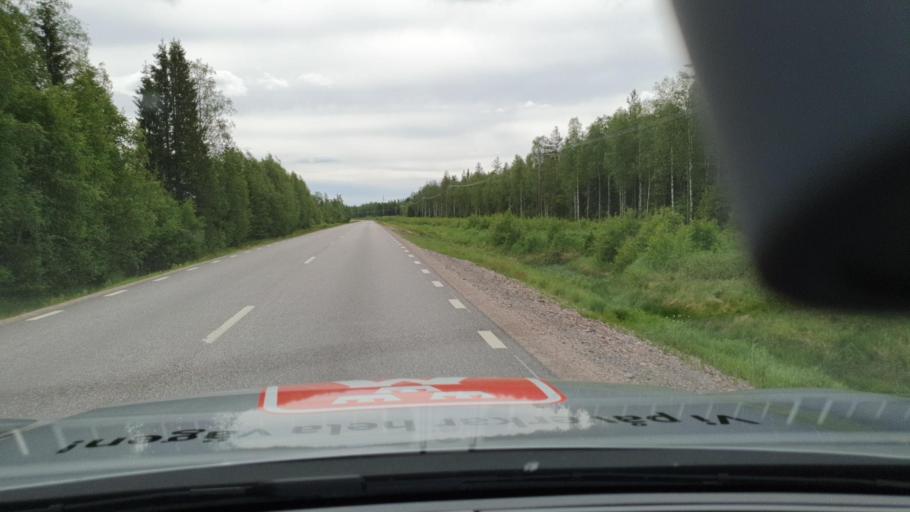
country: SE
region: Norrbotten
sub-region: Kalix Kommun
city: Kalix
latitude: 65.9021
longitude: 23.4593
